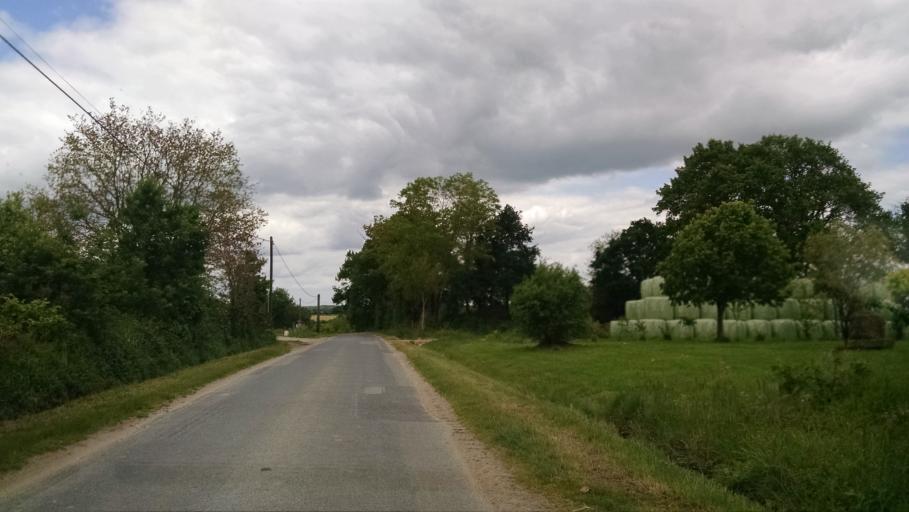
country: FR
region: Pays de la Loire
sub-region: Departement de la Loire-Atlantique
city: Remouille
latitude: 47.0361
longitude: -1.3837
